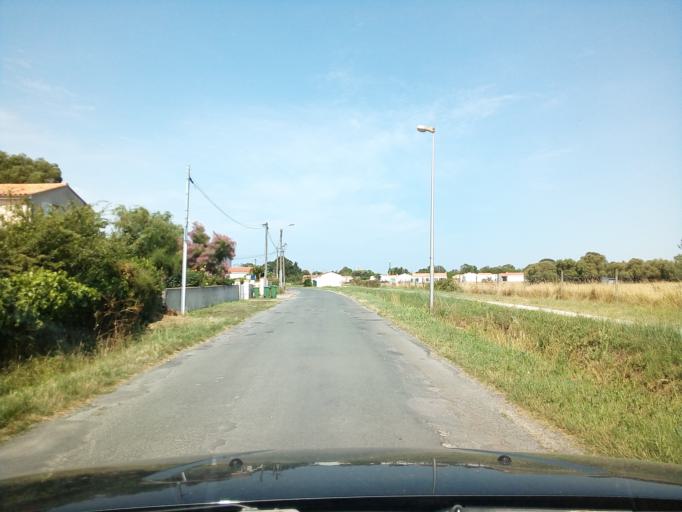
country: FR
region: Poitou-Charentes
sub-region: Departement de la Charente-Maritime
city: Dolus-d'Oleron
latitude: 45.9478
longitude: -1.2969
